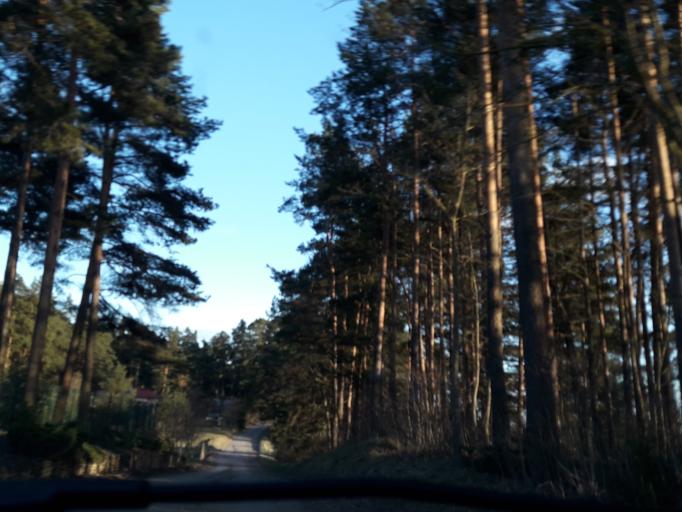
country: LV
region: Kekava
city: Kekava
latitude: 56.8593
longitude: 24.2198
